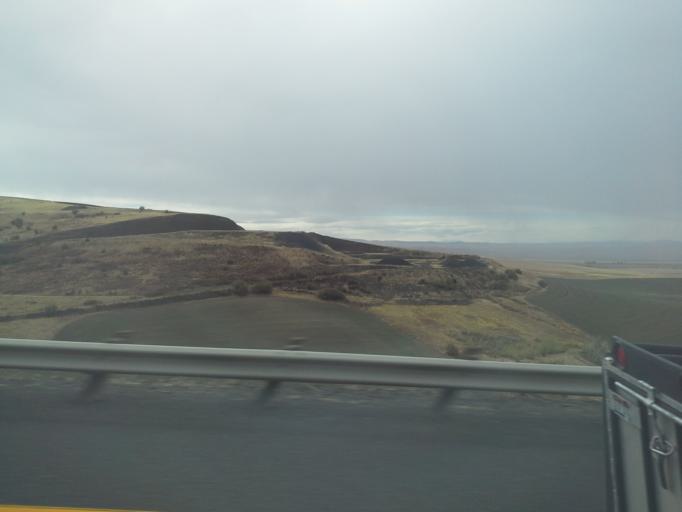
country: US
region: Oregon
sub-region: Umatilla County
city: Mission
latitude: 45.6019
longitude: -118.6431
